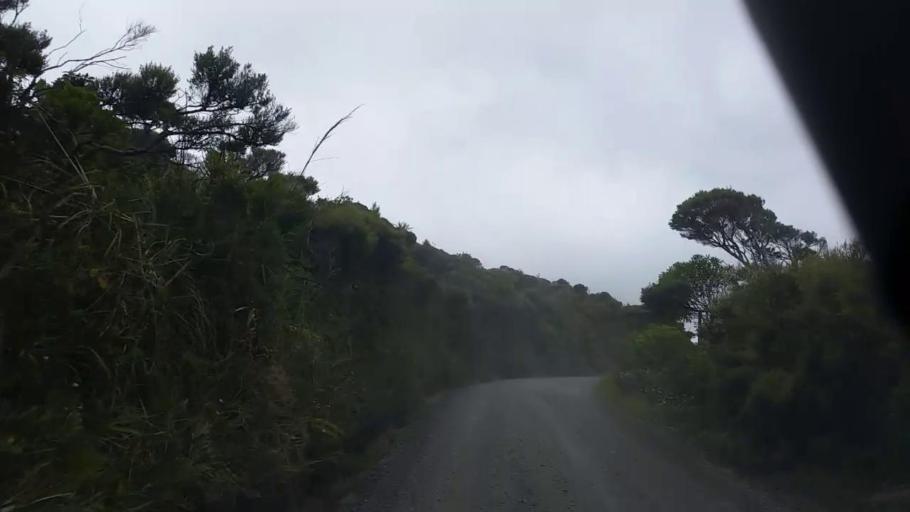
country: NZ
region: Auckland
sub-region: Auckland
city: Muriwai Beach
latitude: -36.9300
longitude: 174.4673
